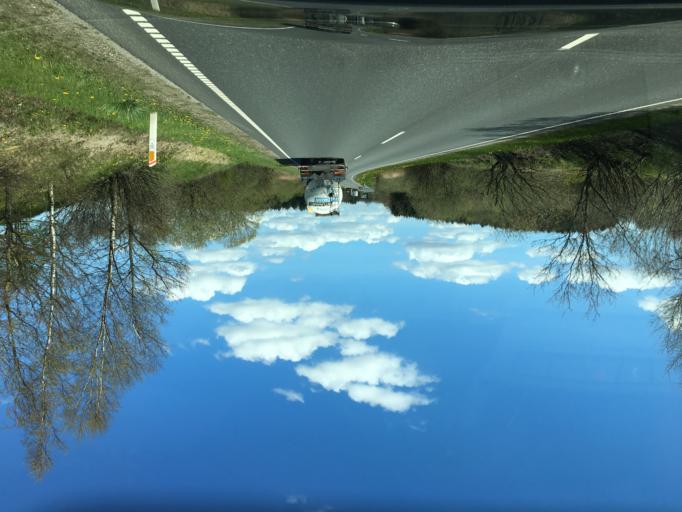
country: DK
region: Central Jutland
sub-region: Hedensted Kommune
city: Hedensted
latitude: 55.8422
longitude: 9.7486
